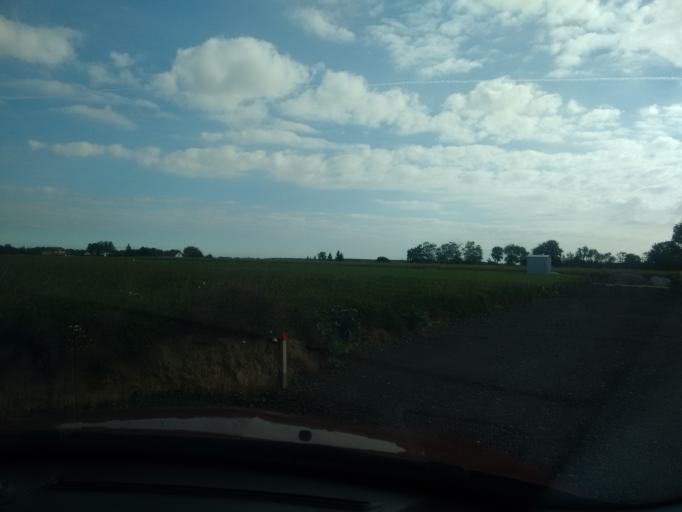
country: AT
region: Upper Austria
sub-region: Wels-Land
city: Steinhaus
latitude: 48.1238
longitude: 14.0202
